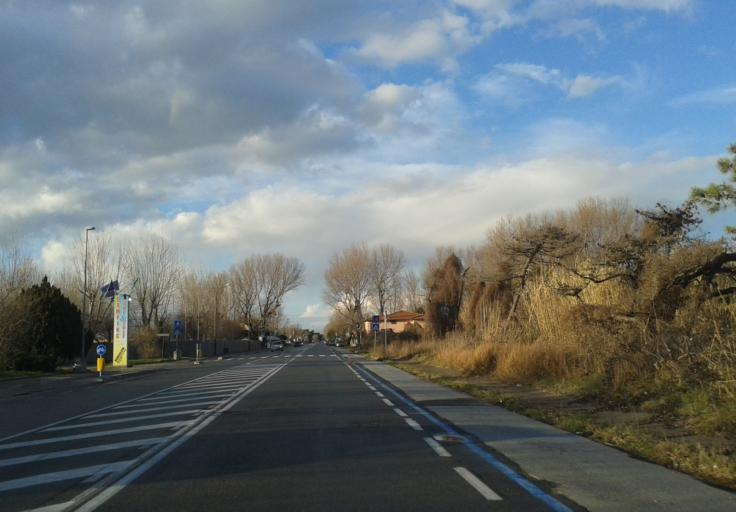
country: IT
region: Tuscany
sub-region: Province of Pisa
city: Marina di Pisa-Tirrenia-Calambrone
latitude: 43.5866
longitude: 10.3002
